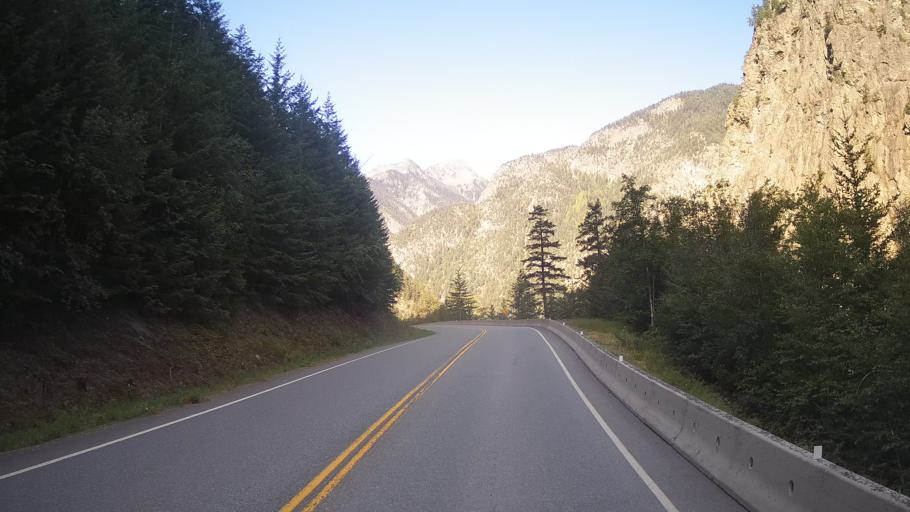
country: CA
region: British Columbia
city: Lillooet
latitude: 50.6411
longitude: -122.0691
